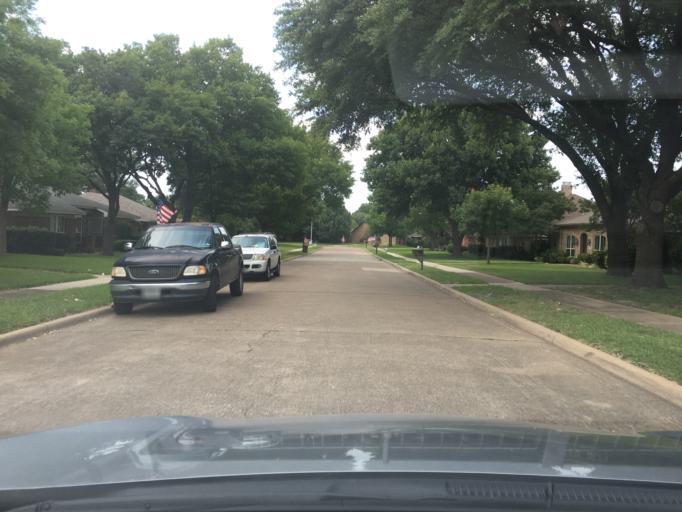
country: US
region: Texas
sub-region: Dallas County
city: Richardson
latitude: 32.9535
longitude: -96.6961
